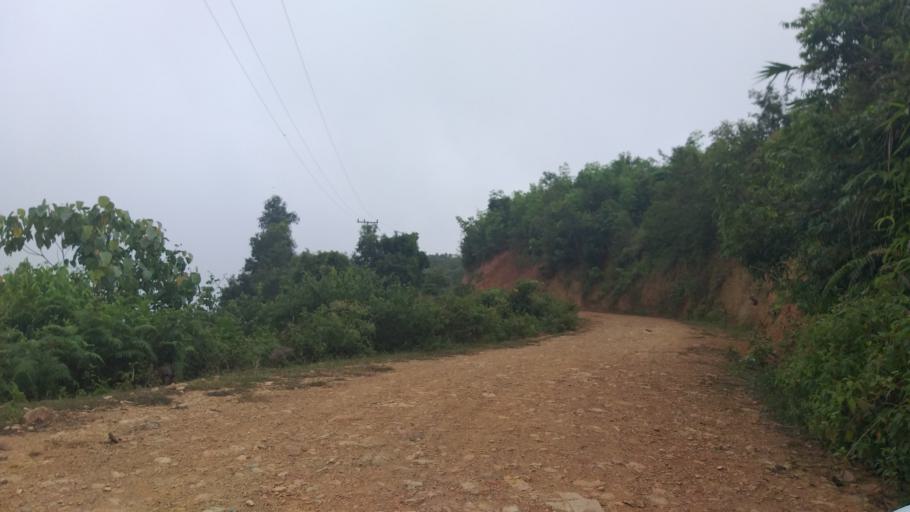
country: LA
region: Phongsali
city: Khoa
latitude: 21.2862
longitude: 102.6420
